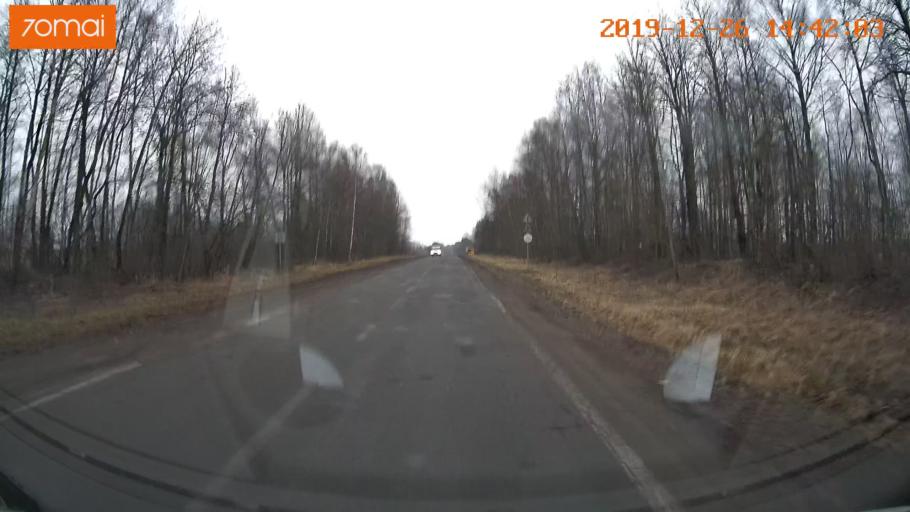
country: RU
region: Jaroslavl
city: Poshekhon'ye
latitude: 58.3667
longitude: 39.0262
